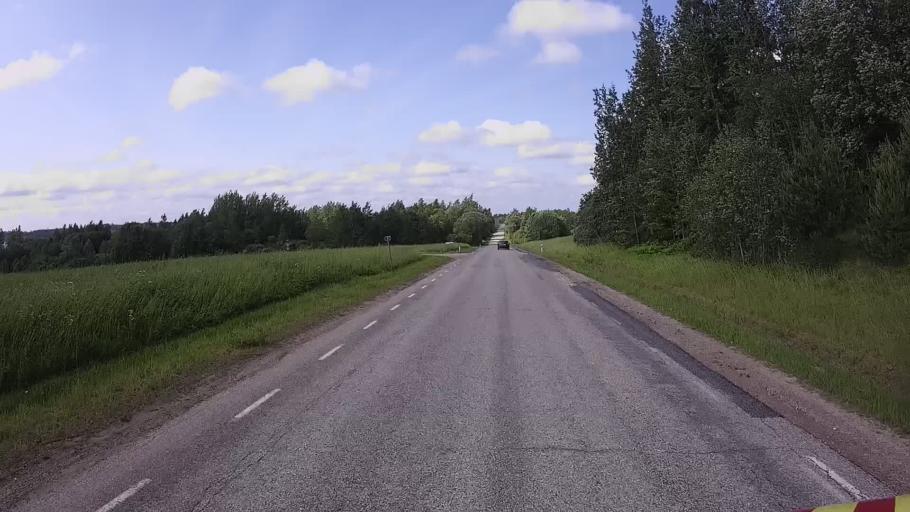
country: EE
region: Vorumaa
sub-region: Antsla vald
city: Vana-Antsla
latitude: 57.8557
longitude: 26.5953
